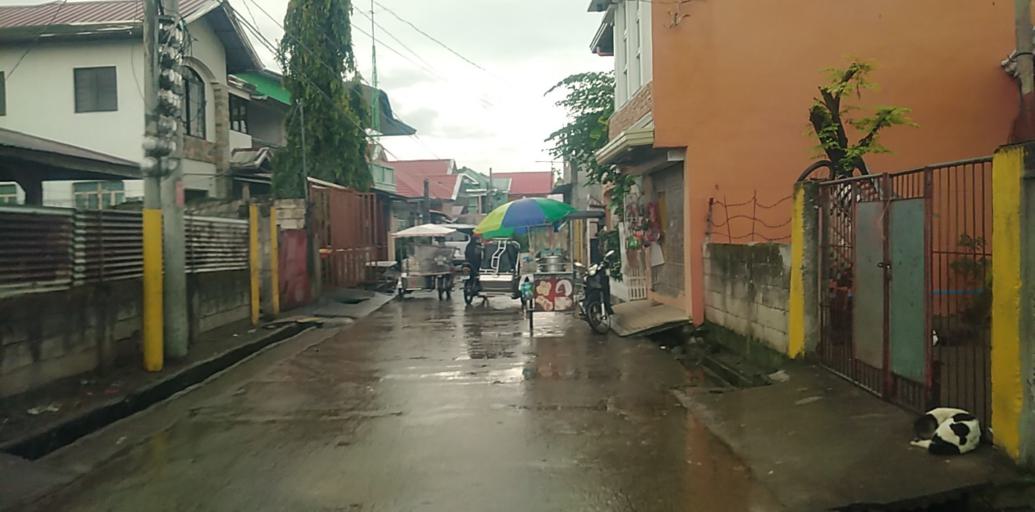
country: PH
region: Central Luzon
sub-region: Province of Pampanga
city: Anao
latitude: 15.1549
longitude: 120.7247
